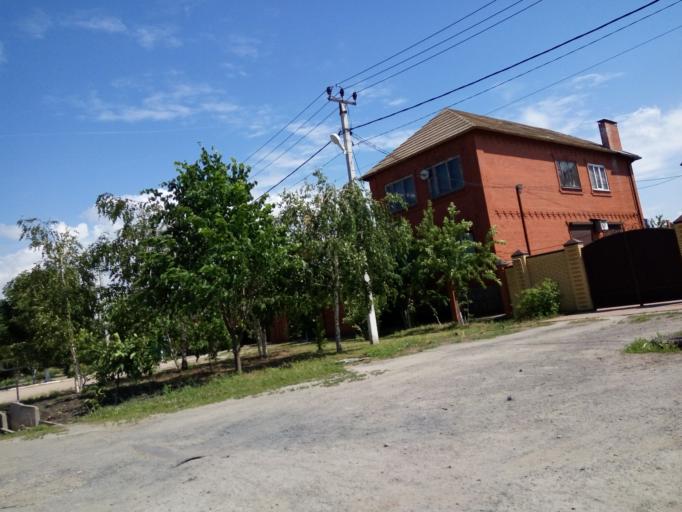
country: RU
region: Rostov
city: Bataysk
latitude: 47.1250
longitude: 39.7454
